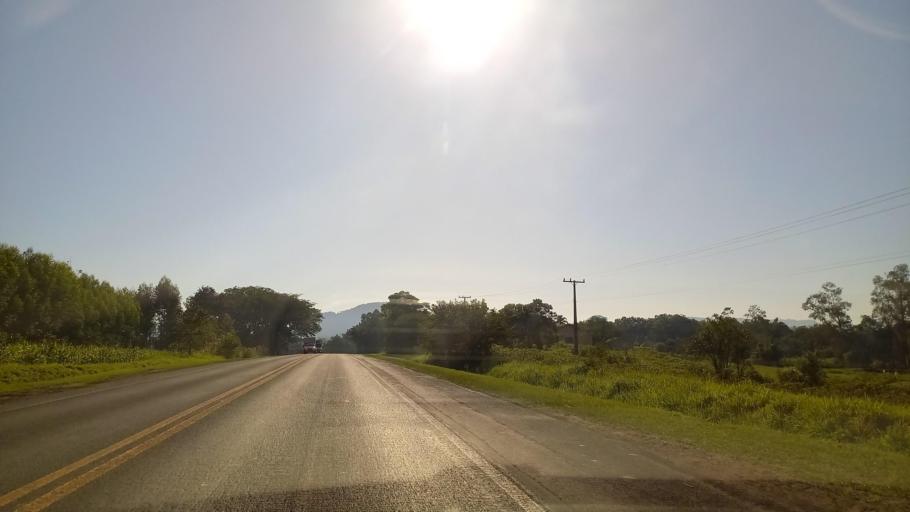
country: BR
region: Rio Grande do Sul
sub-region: Taquari
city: Taquari
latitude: -29.6954
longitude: -51.7482
